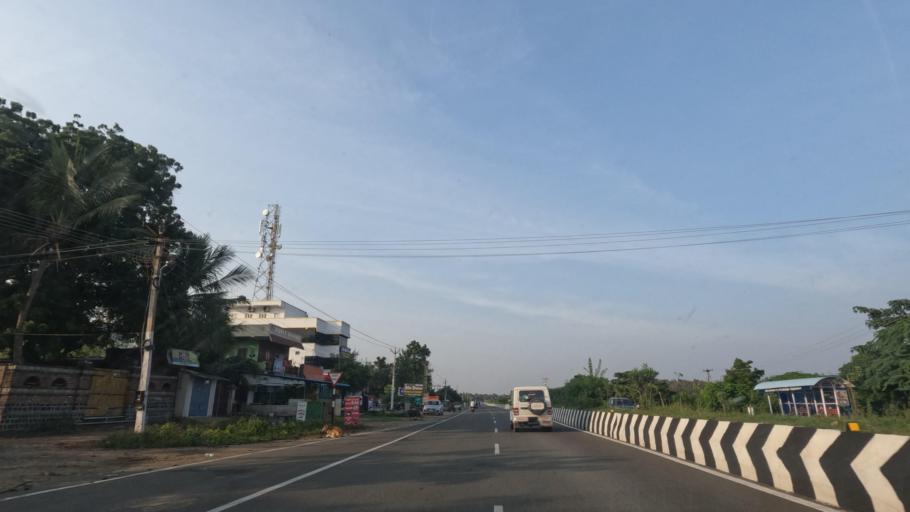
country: IN
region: Tamil Nadu
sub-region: Kancheepuram
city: Mamallapuram
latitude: 12.6616
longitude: 80.2091
